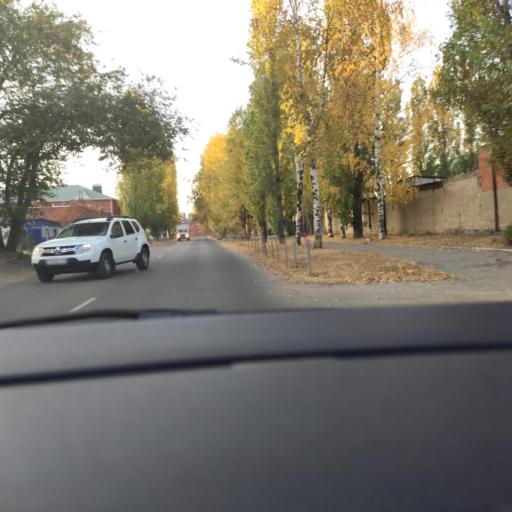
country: RU
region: Voronezj
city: Voronezh
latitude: 51.6599
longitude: 39.1470
